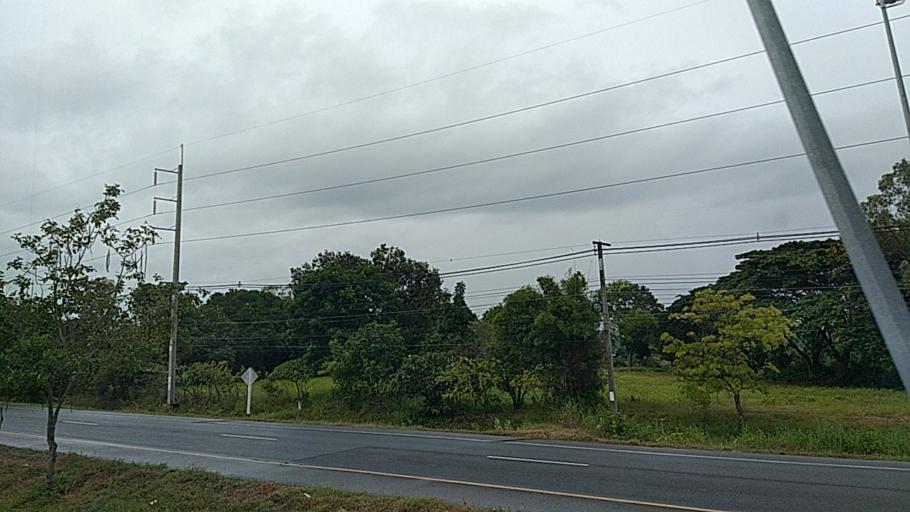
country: TH
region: Maha Sarakham
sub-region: Amphoe Borabue
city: Borabue
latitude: 16.0666
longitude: 103.1448
